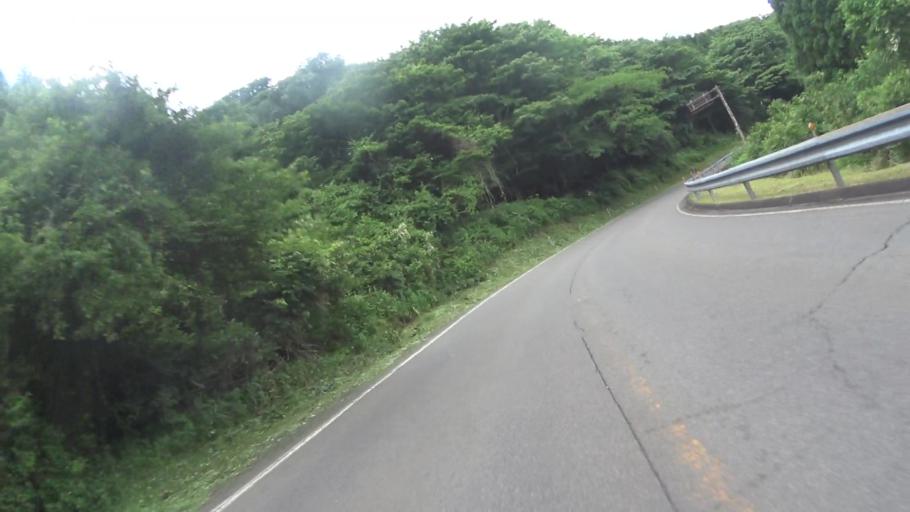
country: JP
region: Oita
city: Tsukawaki
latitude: 33.2420
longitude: 131.2883
